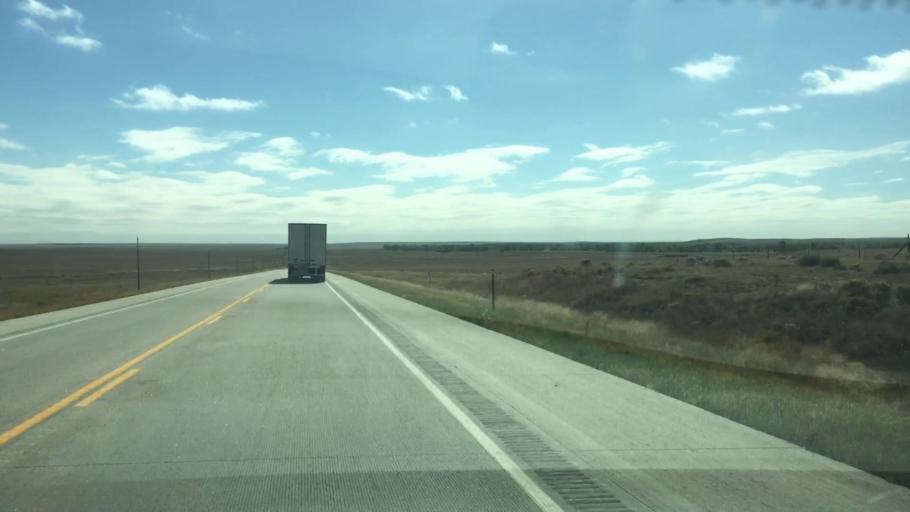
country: US
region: Colorado
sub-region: Lincoln County
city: Hugo
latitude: 39.0750
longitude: -103.3804
